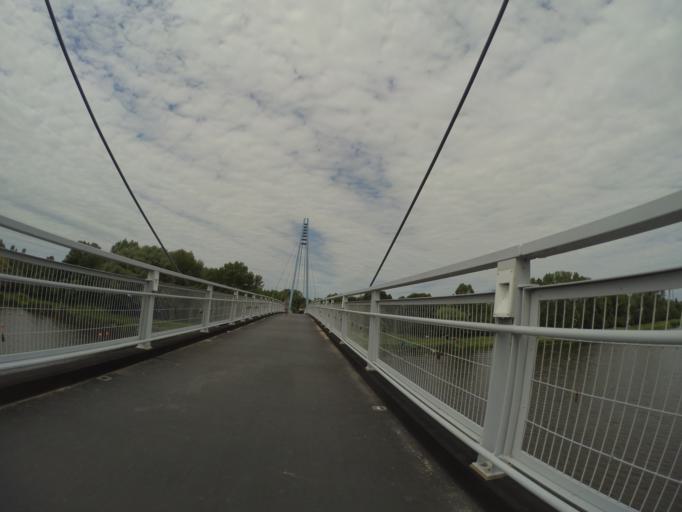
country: CZ
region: Central Bohemia
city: Celakovice
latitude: 50.1701
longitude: 14.7588
